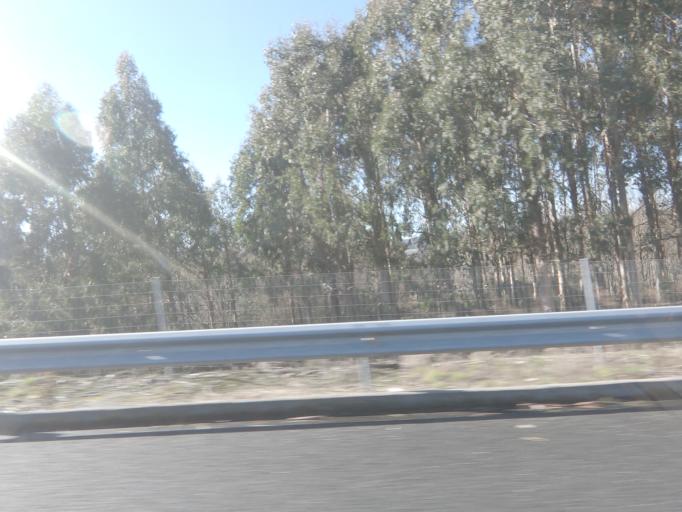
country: ES
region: Galicia
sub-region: Provincia de Pontevedra
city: Dozon
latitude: 42.5857
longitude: -8.0731
